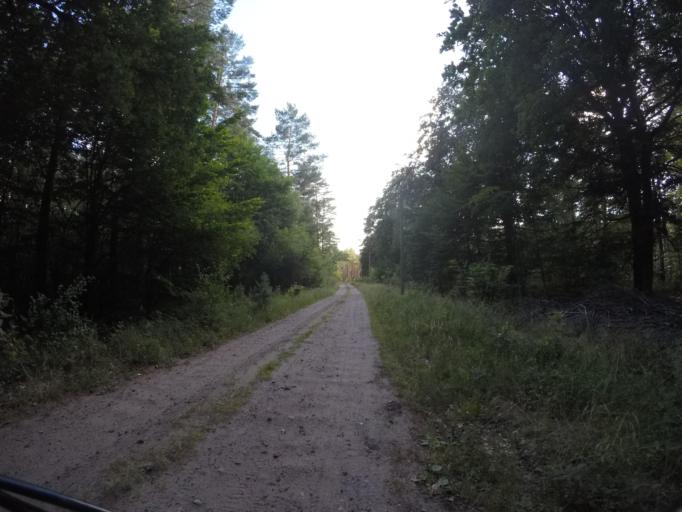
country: DE
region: Mecklenburg-Vorpommern
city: Lubtheen
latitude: 53.2599
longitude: 10.9944
